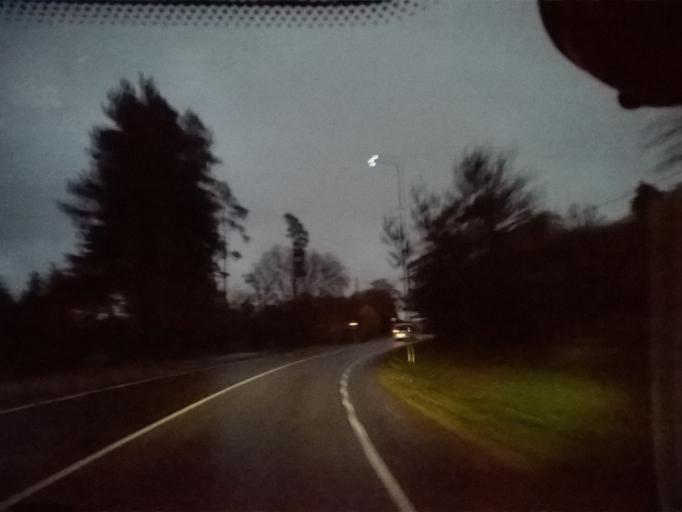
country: EE
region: Harju
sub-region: Viimsi vald
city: Viimsi
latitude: 59.5128
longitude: 24.8518
